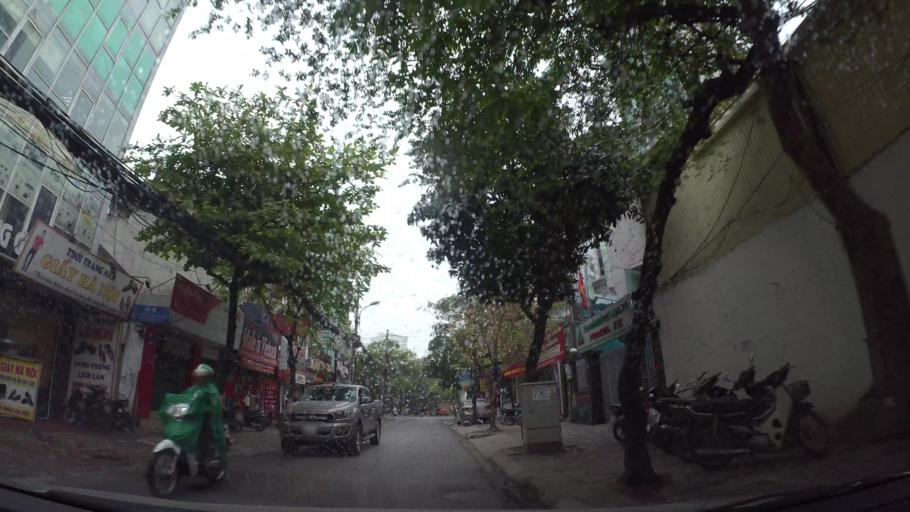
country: VN
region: Ha Noi
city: Thanh Xuan
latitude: 21.0134
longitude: 105.8003
